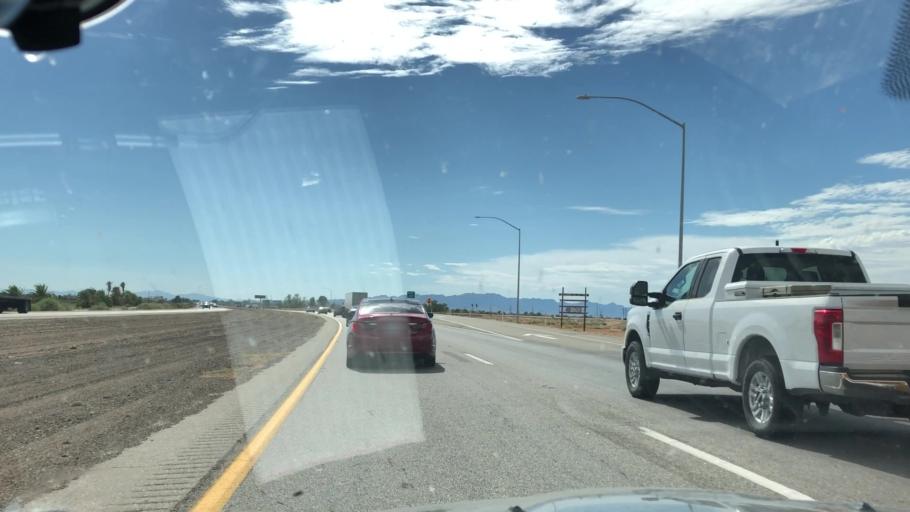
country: US
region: Arizona
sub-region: La Paz County
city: Ehrenberg
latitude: 33.6078
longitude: -114.5434
